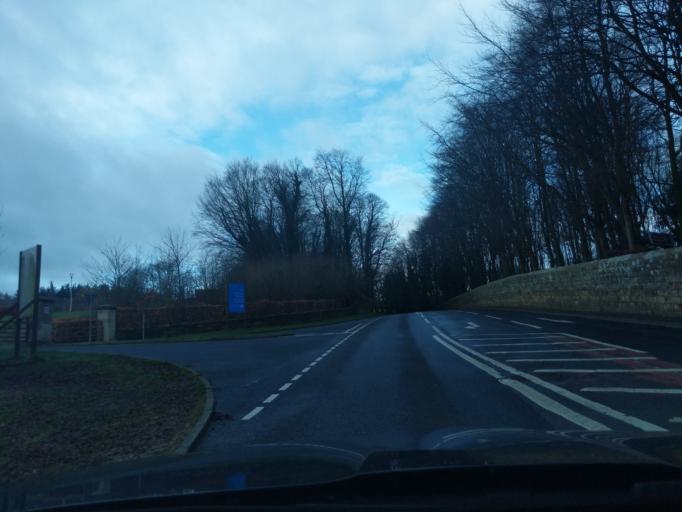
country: GB
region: England
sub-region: Northumberland
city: Alnwick
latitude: 55.4154
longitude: -1.6945
